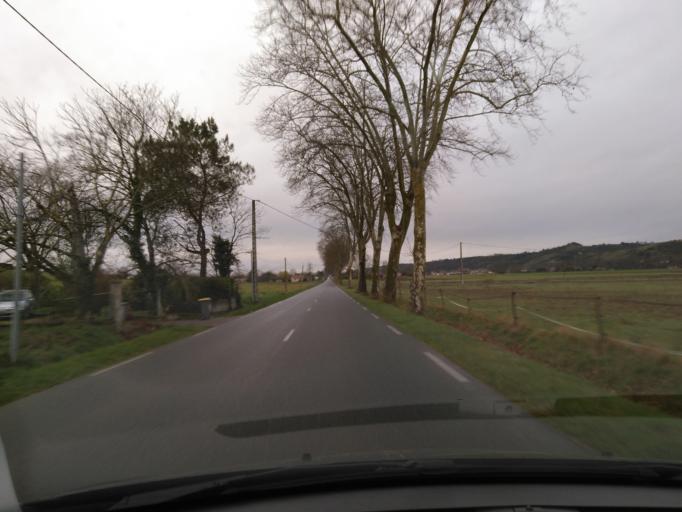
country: FR
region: Midi-Pyrenees
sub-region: Departement de la Haute-Garonne
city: Montesquieu-Volvestre
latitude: 43.1907
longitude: 1.2367
